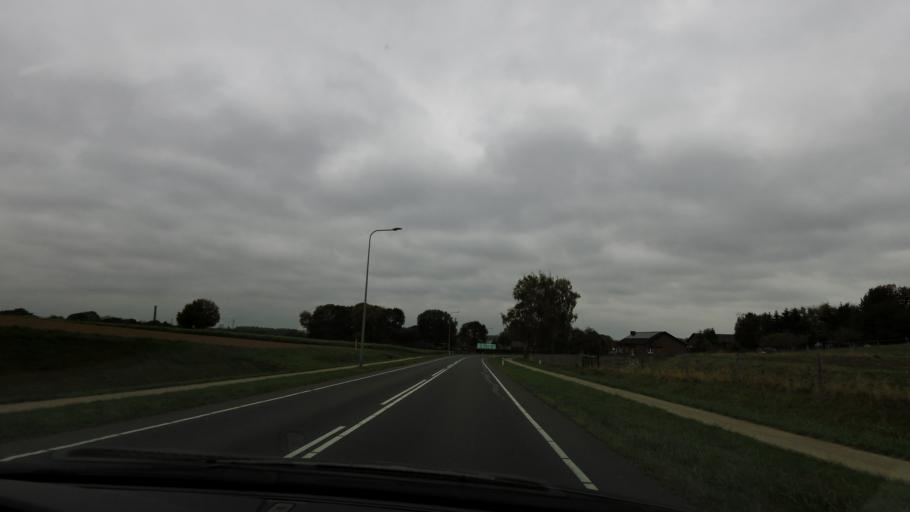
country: NL
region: Limburg
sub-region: Gemeente Schinnen
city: Puth
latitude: 50.9628
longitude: 5.8582
